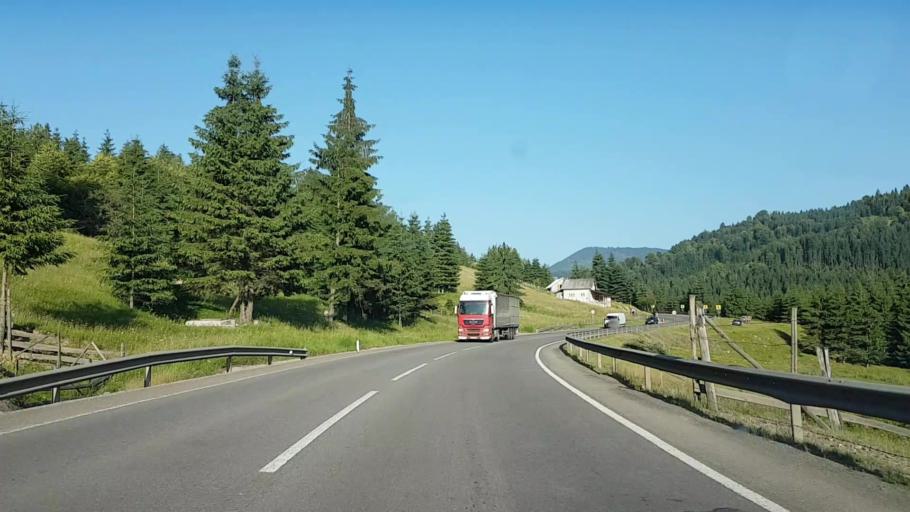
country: RO
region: Bistrita-Nasaud
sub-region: Comuna Tiha Bargaului
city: Tureac
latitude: 47.2229
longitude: 24.9451
